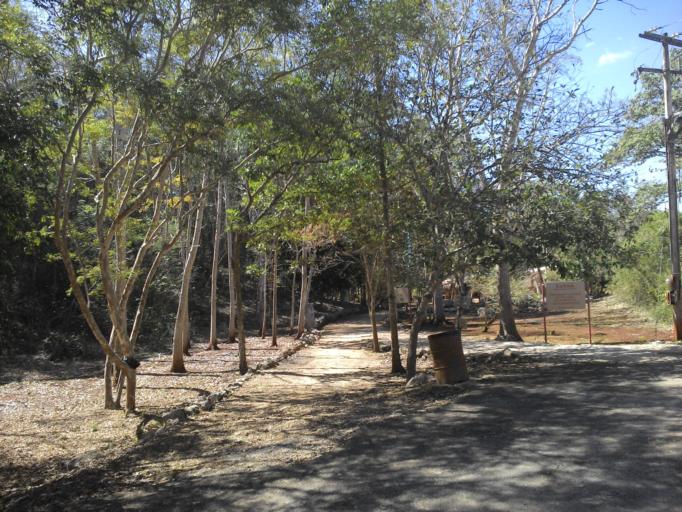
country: MX
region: Yucatan
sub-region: Oxkutzcab
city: Xul
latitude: 20.1749
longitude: -89.5789
